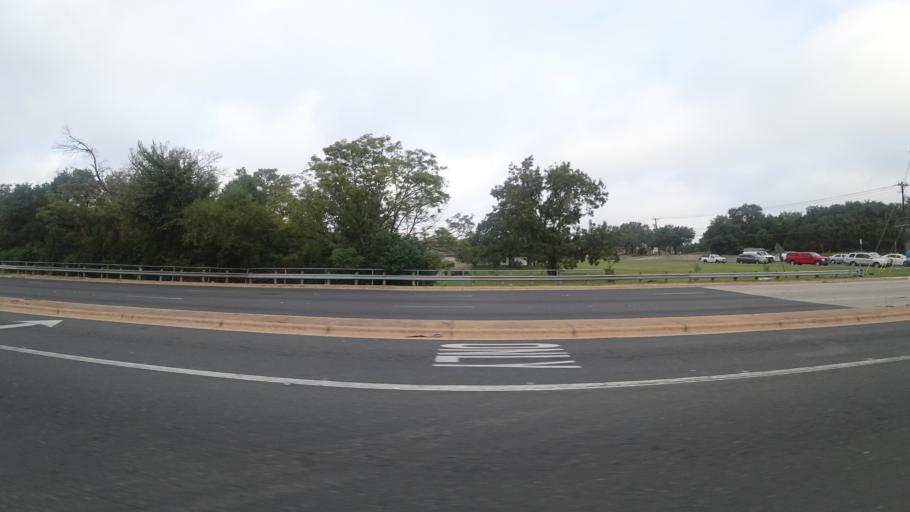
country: US
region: Texas
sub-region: Travis County
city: Wells Branch
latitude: 30.3718
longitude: -97.6662
